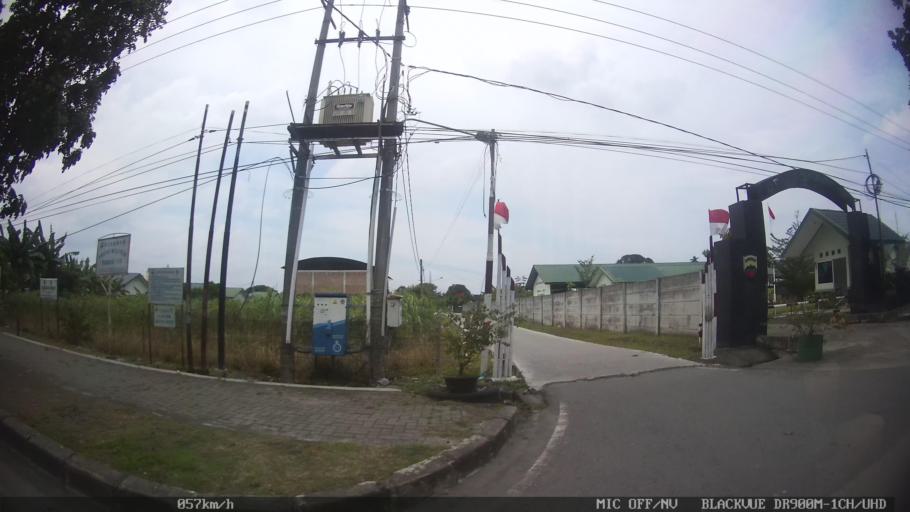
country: ID
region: North Sumatra
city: Medan
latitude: 3.6301
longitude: 98.6768
